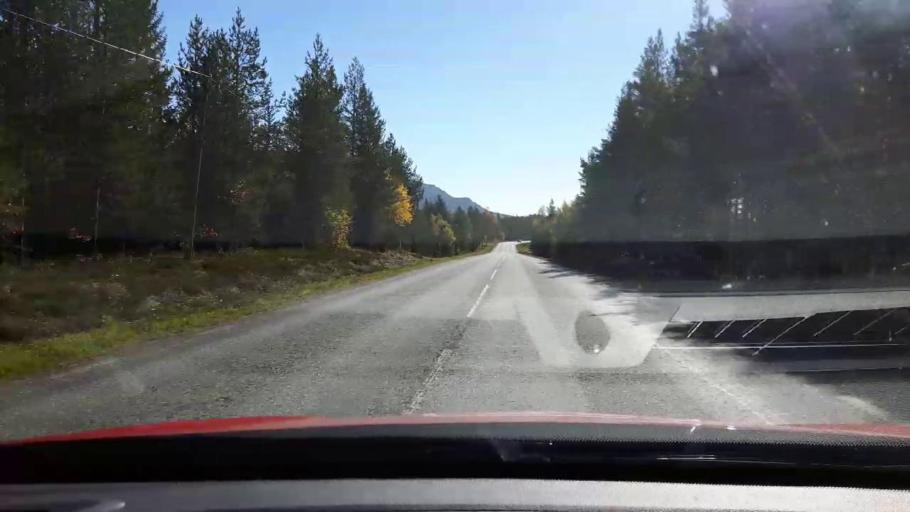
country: SE
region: Jaemtland
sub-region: Harjedalens Kommun
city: Sveg
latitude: 62.4321
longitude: 13.8858
